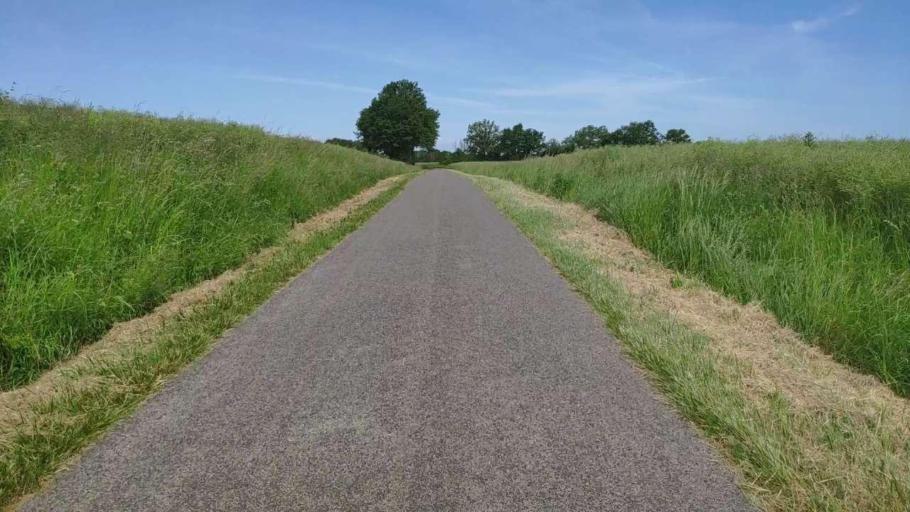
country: FR
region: Franche-Comte
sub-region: Departement du Jura
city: Bletterans
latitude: 46.6865
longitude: 5.4088
